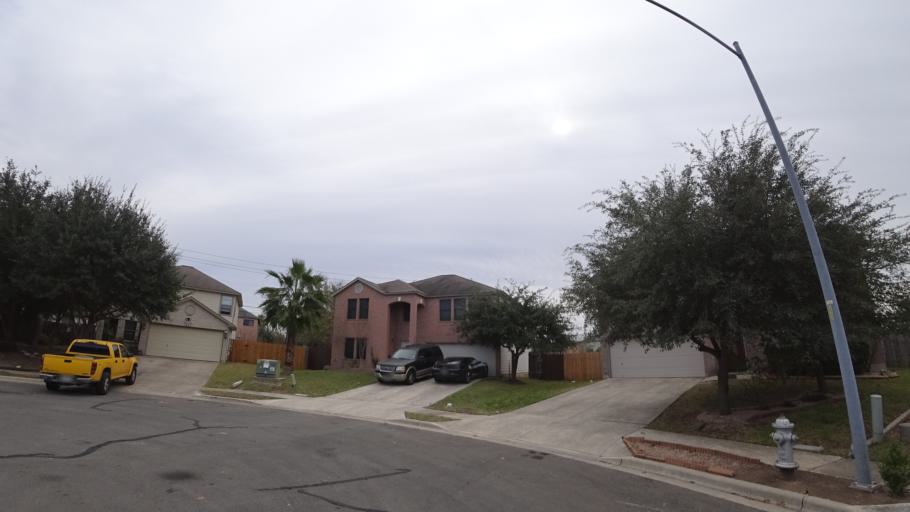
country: US
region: Texas
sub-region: Travis County
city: Onion Creek
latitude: 30.1580
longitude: -97.7412
